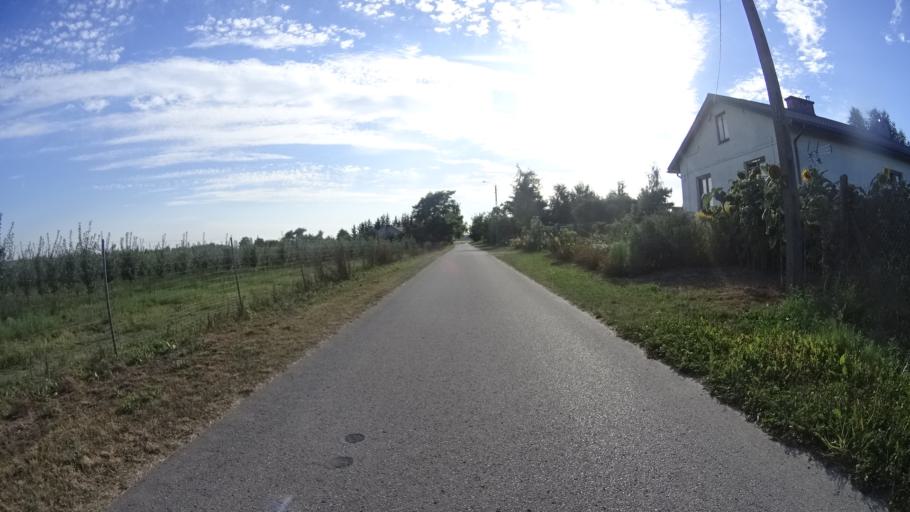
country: PL
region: Masovian Voivodeship
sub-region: Powiat grojecki
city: Goszczyn
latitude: 51.6835
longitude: 20.8323
